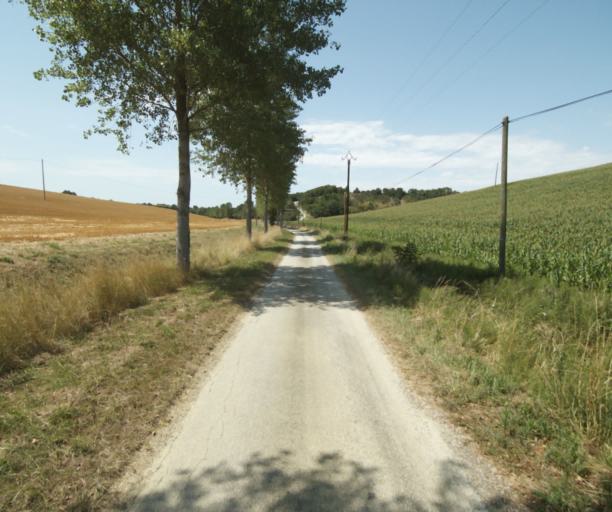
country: FR
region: Midi-Pyrenees
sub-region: Departement de la Haute-Garonne
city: Saint-Felix-Lauragais
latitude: 43.4628
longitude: 1.8620
